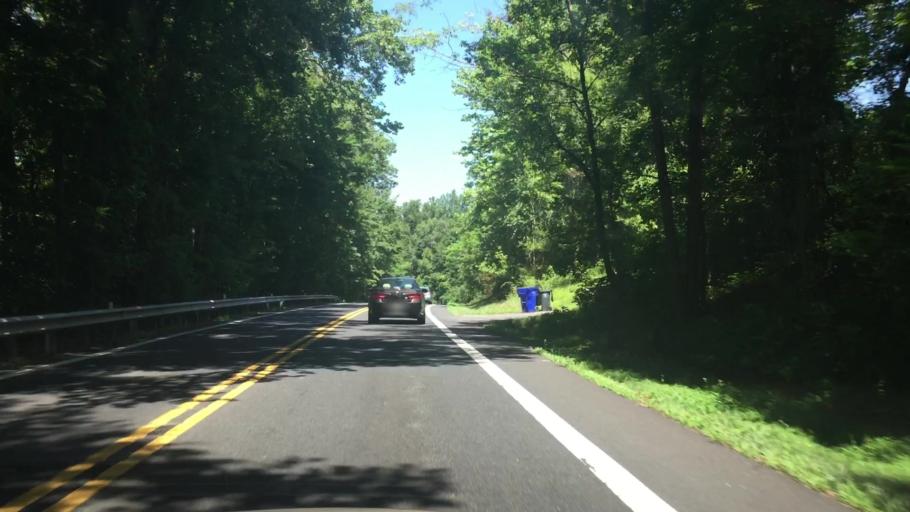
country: US
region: Maryland
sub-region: Harford County
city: Aberdeen
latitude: 39.6145
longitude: -76.2001
